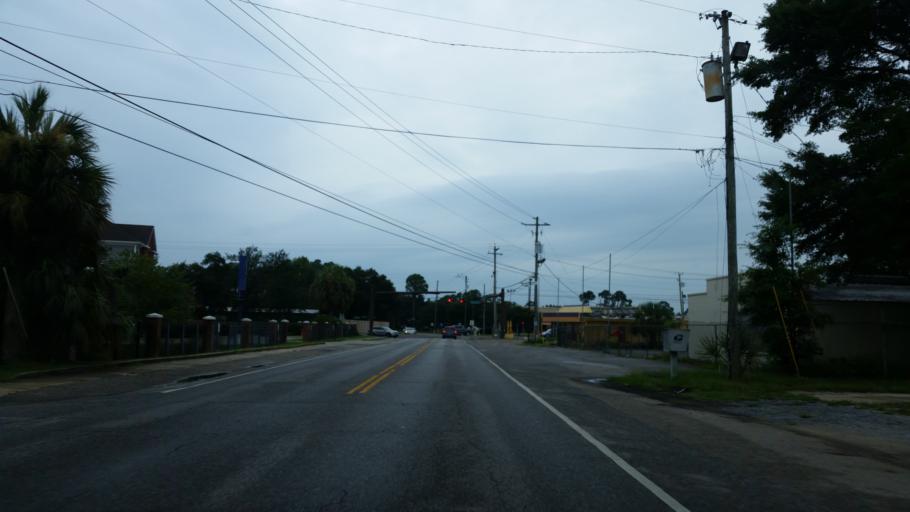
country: US
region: Florida
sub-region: Escambia County
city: Warrington
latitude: 30.3900
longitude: -87.2729
